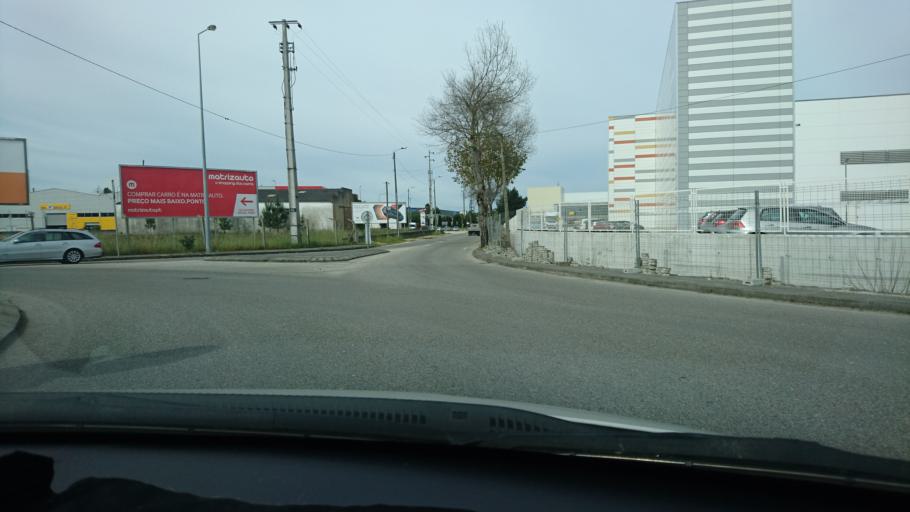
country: PT
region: Aveiro
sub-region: Aveiro
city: Eixo
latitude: 40.6463
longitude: -8.6022
